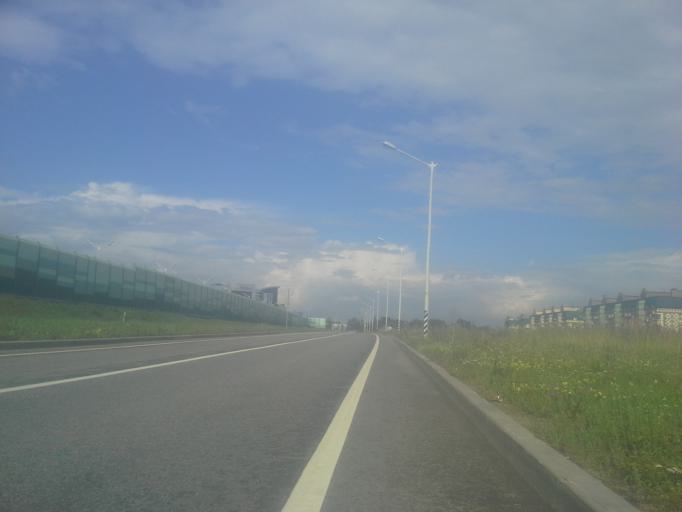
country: RU
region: Moskovskaya
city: Lesnoy Gorodok
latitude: 55.6281
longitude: 37.2045
